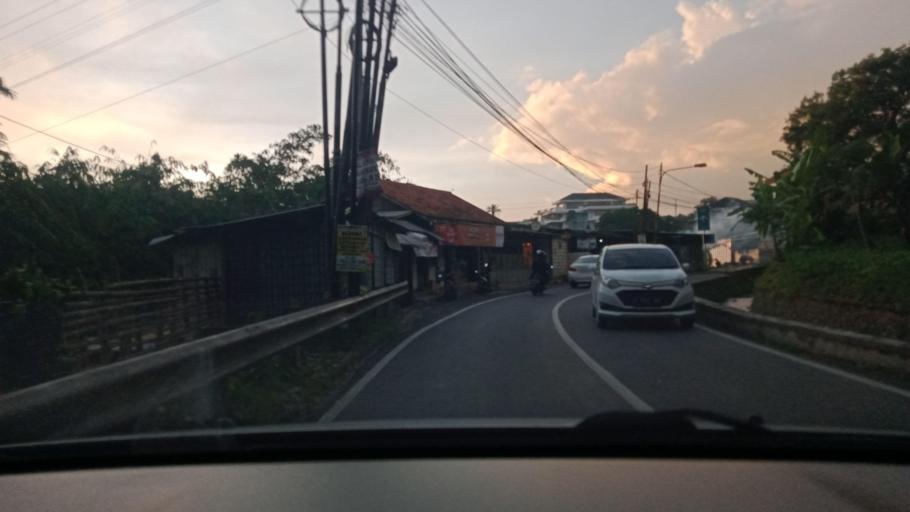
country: ID
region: West Java
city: Lembang
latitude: -6.8512
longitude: 107.5908
